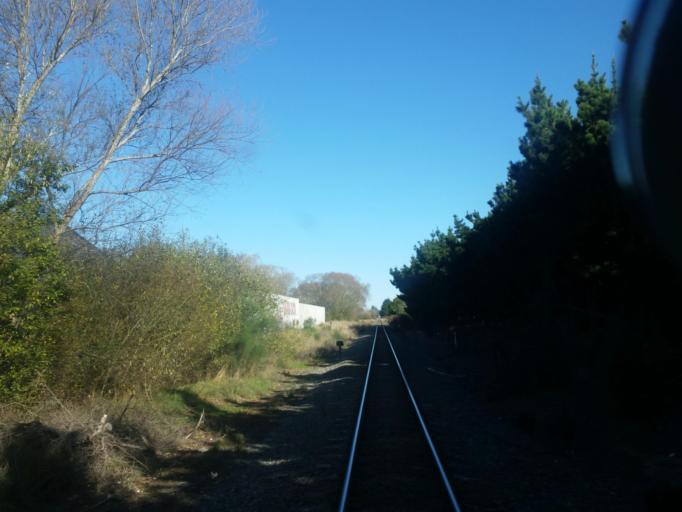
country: NZ
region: Canterbury
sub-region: Waimakariri District
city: Kaiapoi
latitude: -43.3930
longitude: 172.6568
